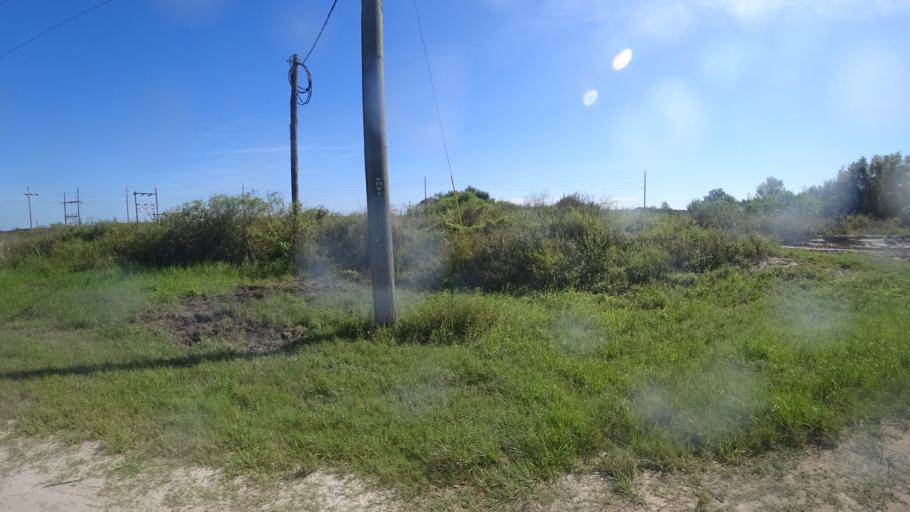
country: US
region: Florida
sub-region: Hillsborough County
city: Balm
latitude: 27.6467
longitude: -82.1209
